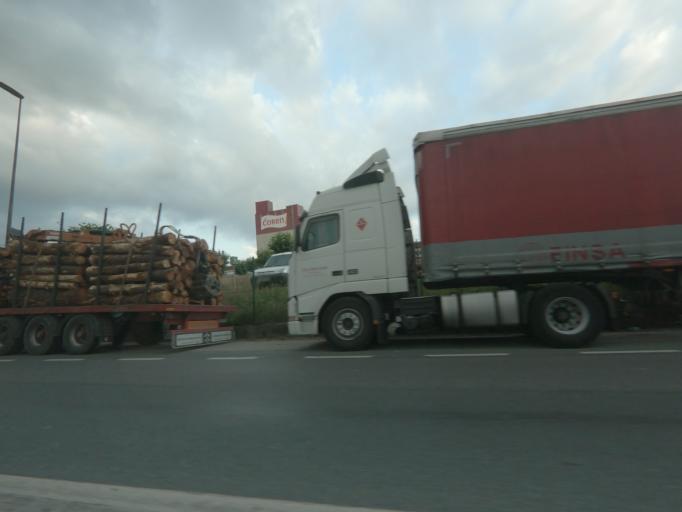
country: ES
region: Galicia
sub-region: Provincia de Ourense
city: Taboadela
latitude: 42.2889
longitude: -7.8228
